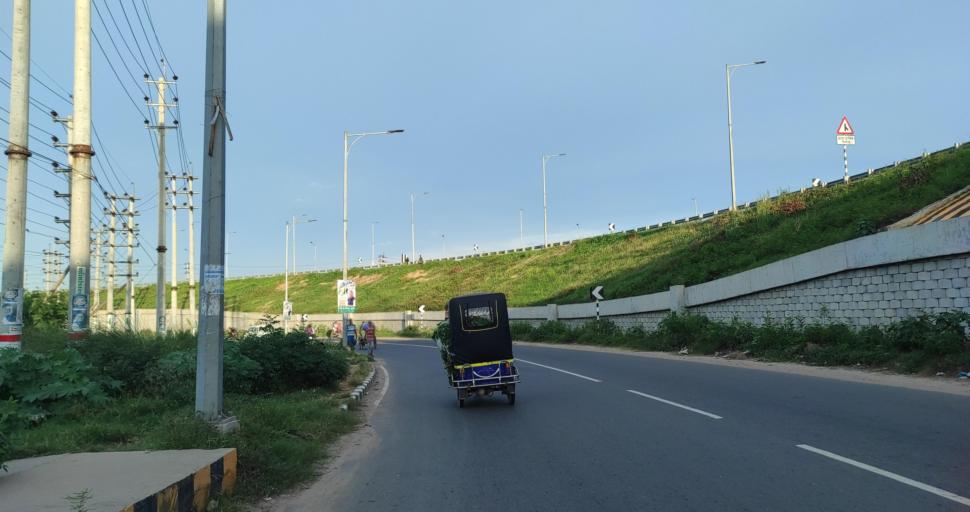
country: BD
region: Dhaka
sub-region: Dhaka
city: Dhaka
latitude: 23.6764
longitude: 90.4048
